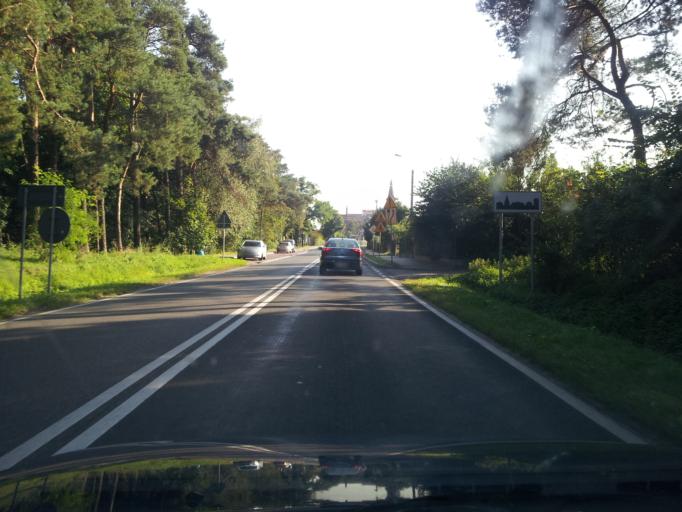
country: PL
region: Masovian Voivodeship
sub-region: Powiat warszawski zachodni
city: Leszno
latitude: 52.2615
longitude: 20.5929
